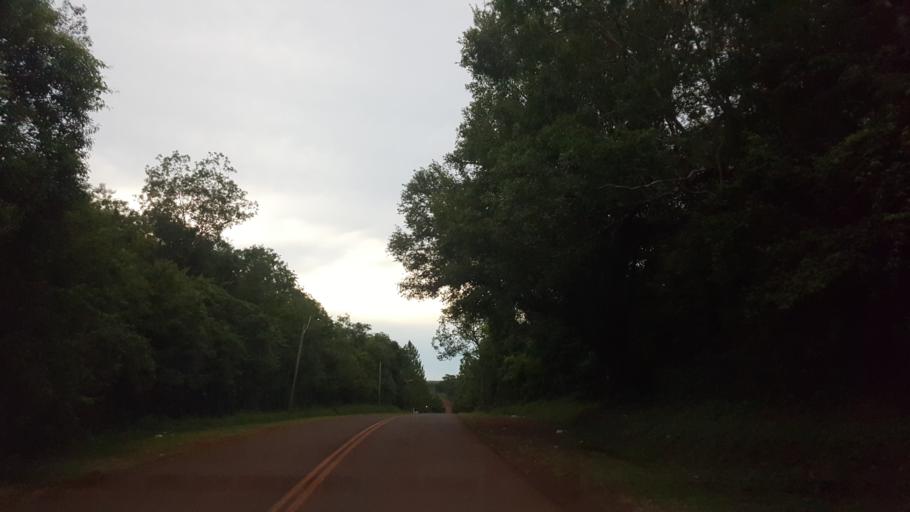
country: AR
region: Misiones
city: Santo Pipo
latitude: -27.1163
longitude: -55.3685
